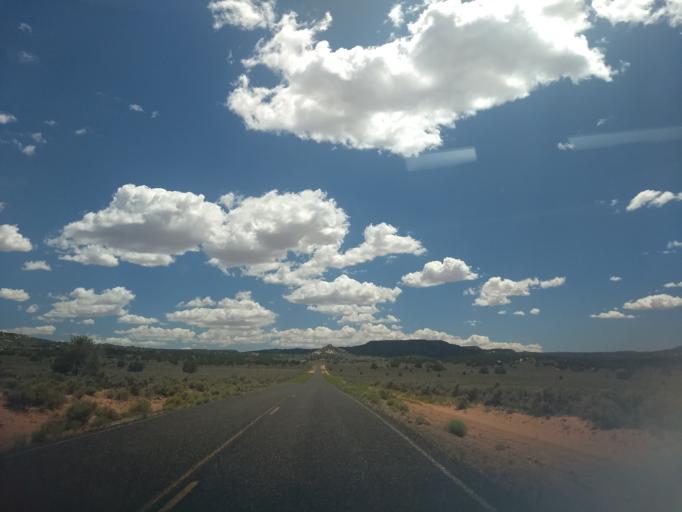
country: US
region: Utah
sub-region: Kane County
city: Kanab
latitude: 37.1580
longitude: -112.6683
